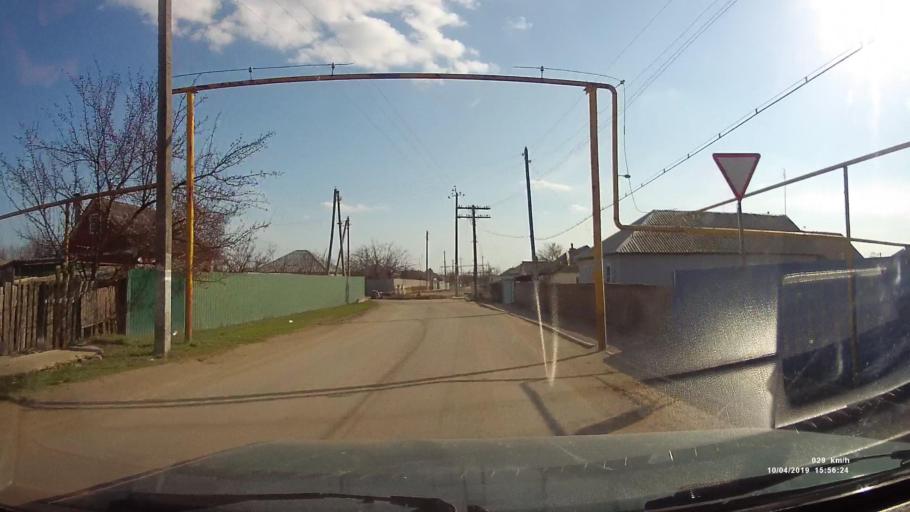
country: RU
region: Rostov
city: Masalovka
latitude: 48.4118
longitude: 40.2705
